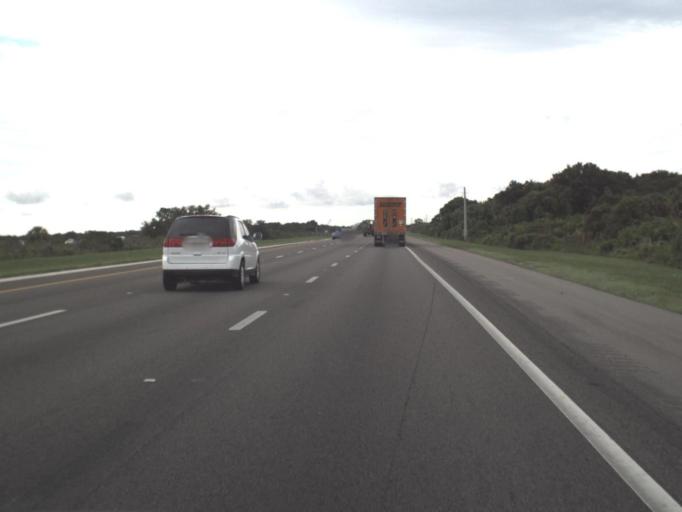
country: US
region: Florida
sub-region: Sarasota County
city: Laurel
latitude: 27.1864
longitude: -82.4380
